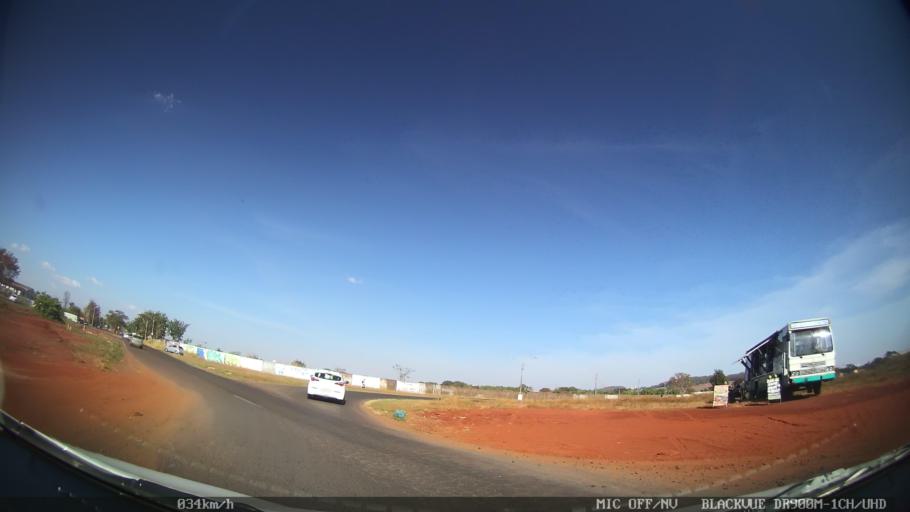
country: BR
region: Sao Paulo
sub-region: Ribeirao Preto
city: Ribeirao Preto
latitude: -21.1456
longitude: -47.7704
